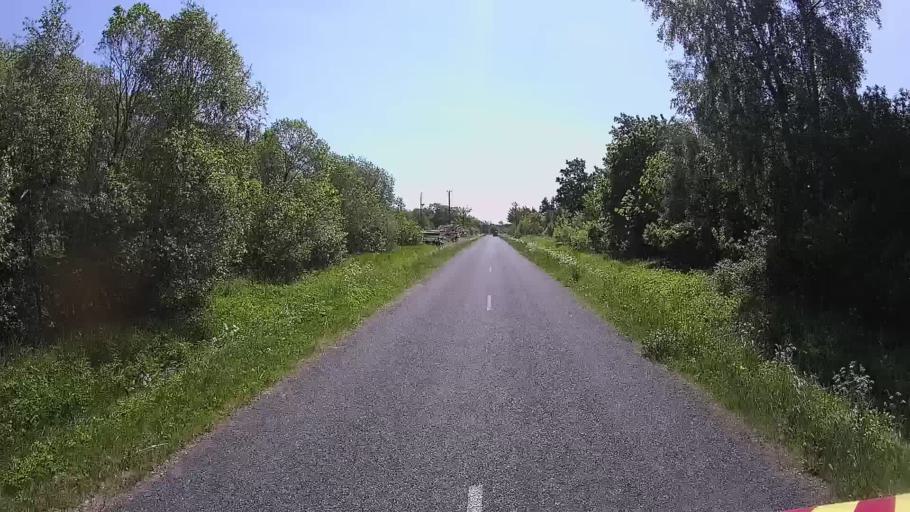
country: LV
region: Dundaga
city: Dundaga
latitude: 57.9404
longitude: 22.0892
